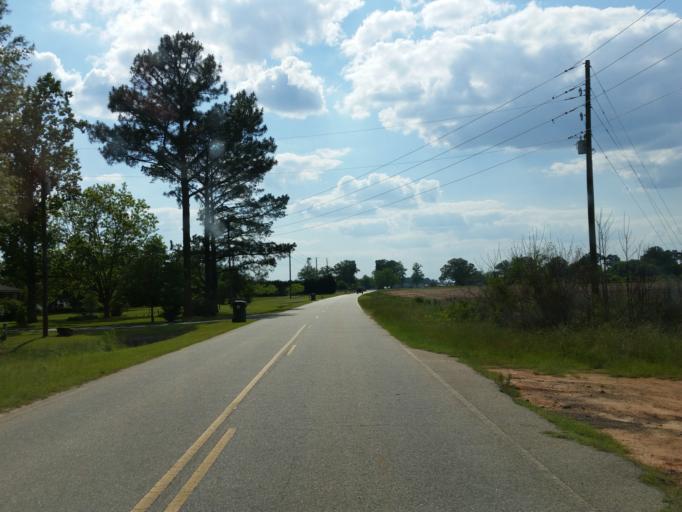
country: US
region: Georgia
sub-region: Houston County
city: Centerville
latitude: 32.5783
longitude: -83.7224
